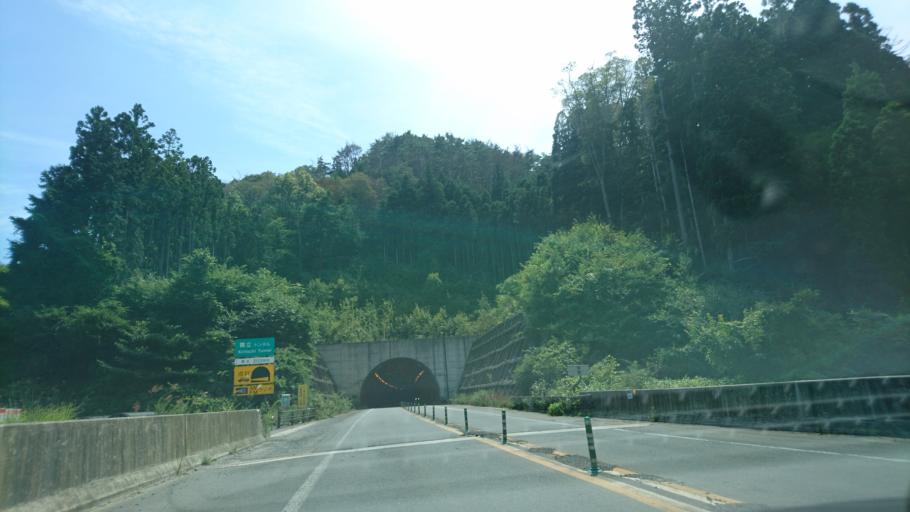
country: JP
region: Iwate
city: Ofunato
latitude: 38.9500
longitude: 141.6282
